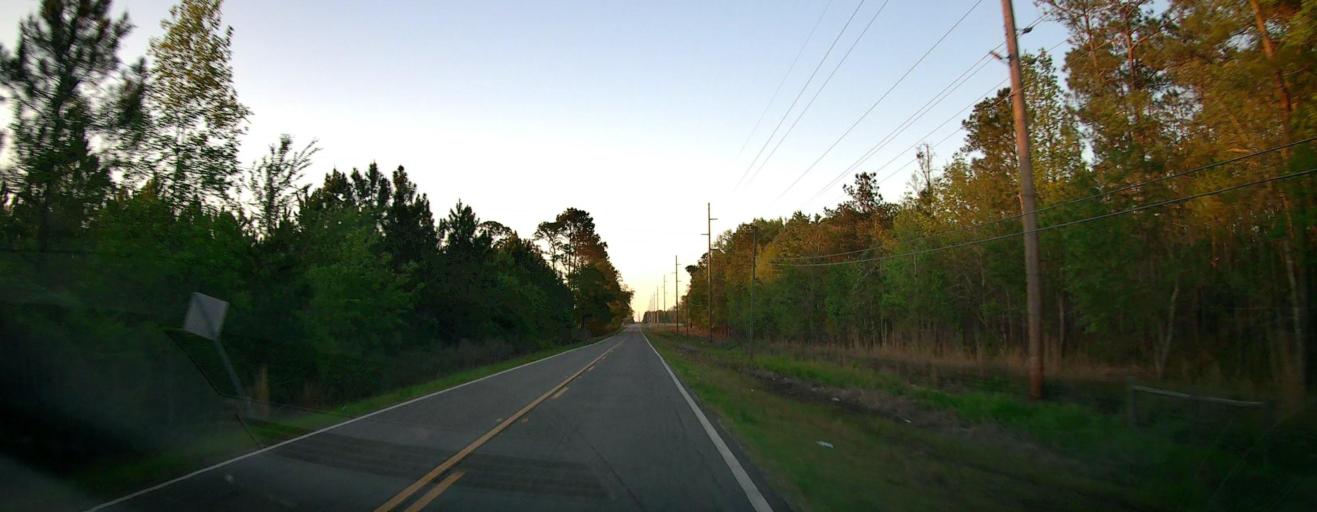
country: US
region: Georgia
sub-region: Ben Hill County
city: Fitzgerald
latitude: 31.7608
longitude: -83.3552
